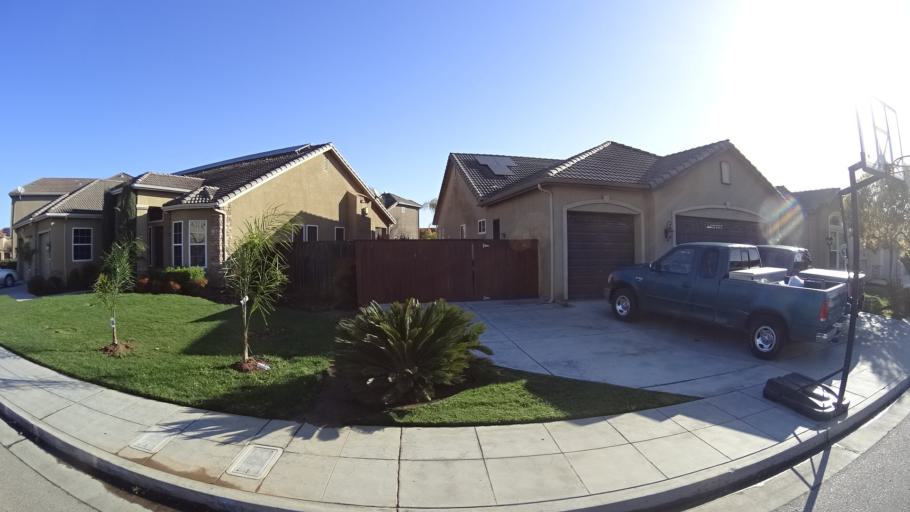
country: US
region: California
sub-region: Fresno County
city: Biola
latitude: 36.8319
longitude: -119.9043
